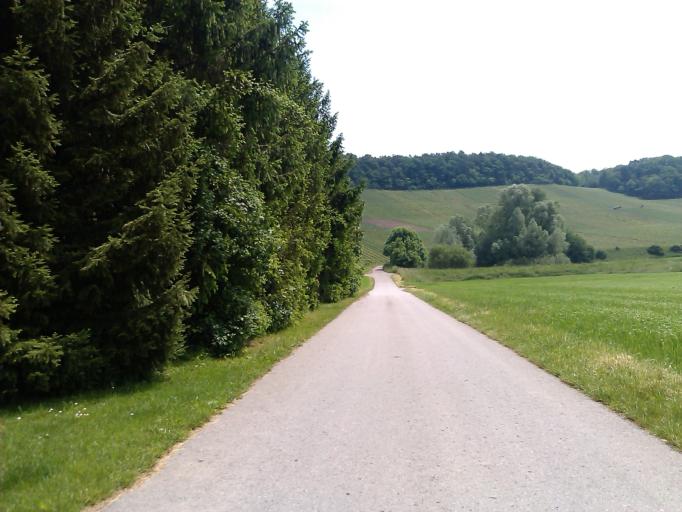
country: DE
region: Baden-Wuerttemberg
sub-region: Regierungsbezirk Stuttgart
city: Pfaffenhofen
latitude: 49.1030
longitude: 8.9823
